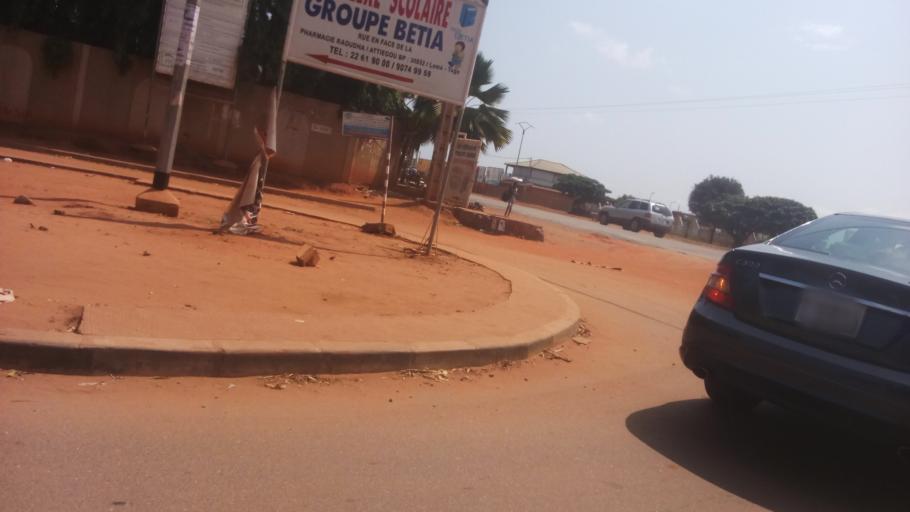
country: TG
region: Maritime
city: Lome
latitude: 6.1948
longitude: 1.2389
